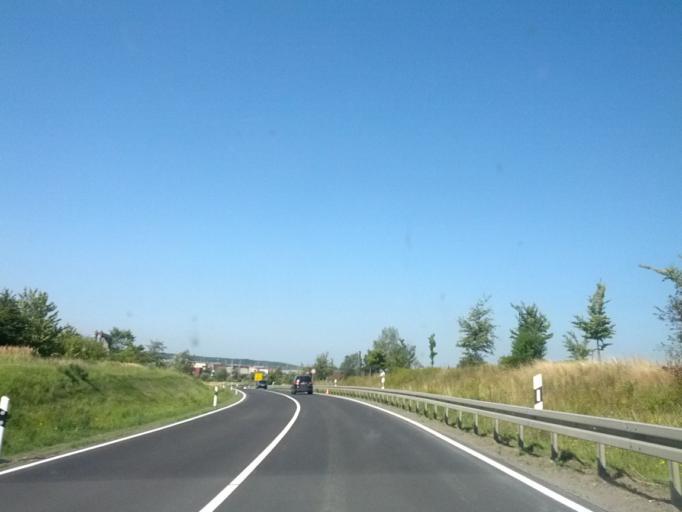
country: DE
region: Mecklenburg-Vorpommern
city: Sagard
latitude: 54.4962
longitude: 13.5713
